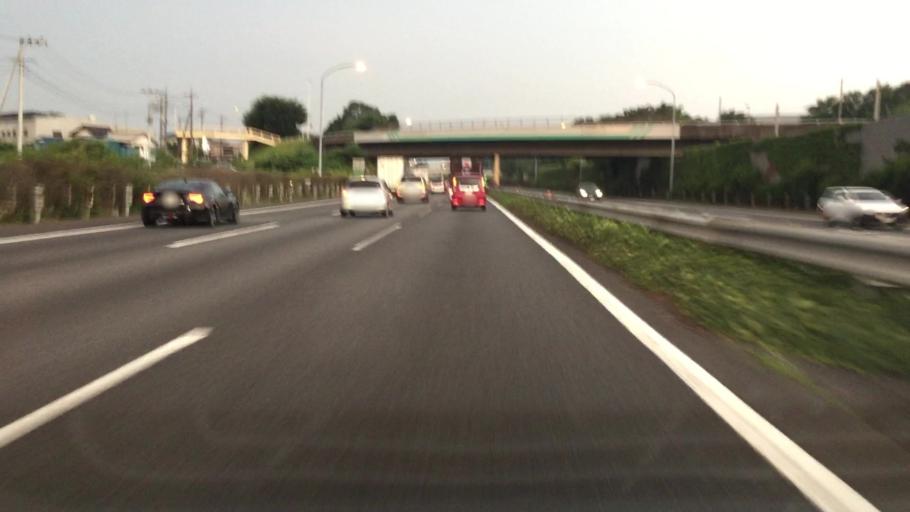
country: JP
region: Saitama
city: Hasuda
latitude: 35.9748
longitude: 139.6658
